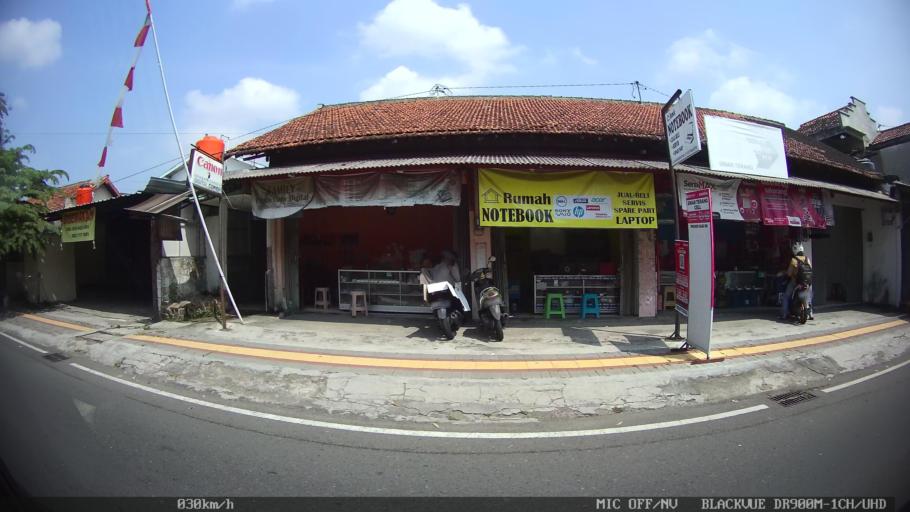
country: ID
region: Daerah Istimewa Yogyakarta
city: Yogyakarta
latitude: -7.8029
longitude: 110.3890
